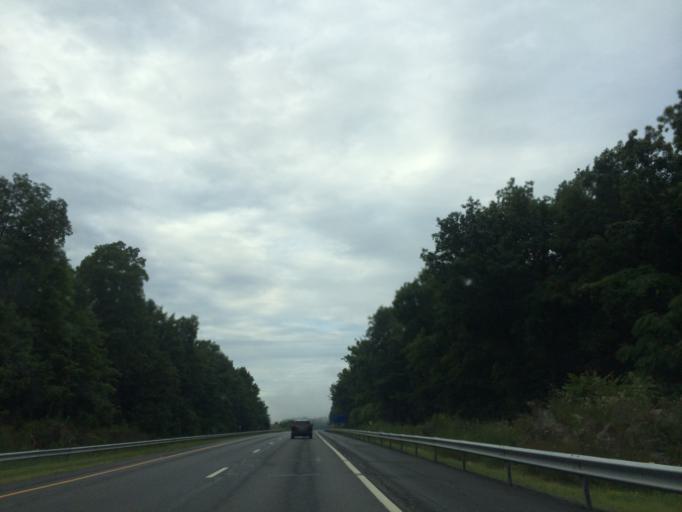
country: US
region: New York
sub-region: Greene County
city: Jefferson Heights
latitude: 42.2683
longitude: -73.8755
